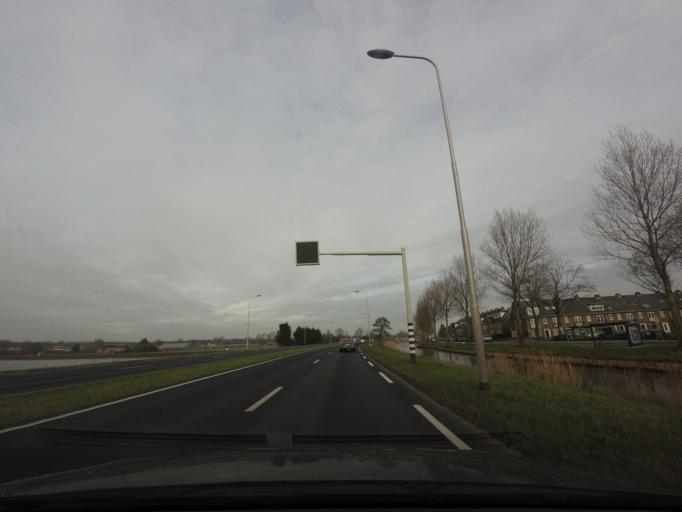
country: NL
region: North Holland
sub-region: Gemeente Haarlem
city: Haarlem
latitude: 52.3755
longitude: 4.6109
